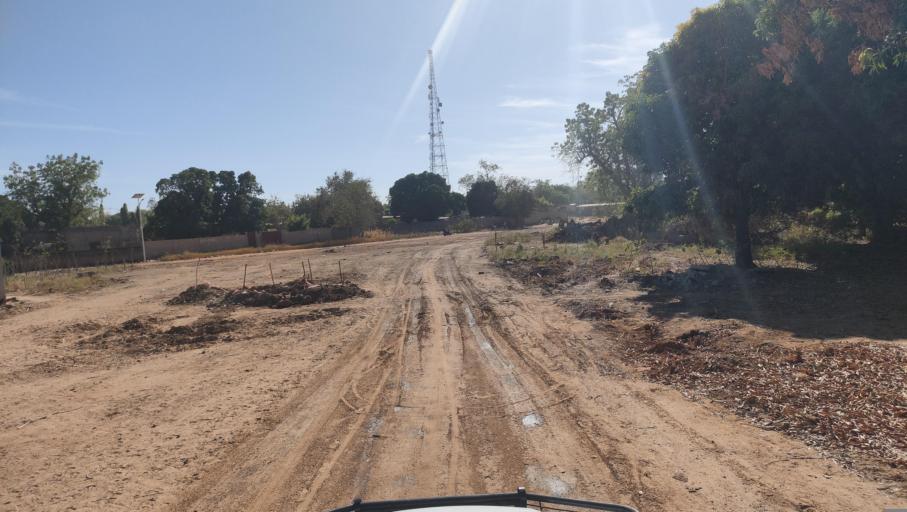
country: BF
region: Est
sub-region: Province du Gourma
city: Fada N'gourma
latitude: 12.0660
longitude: 0.3685
